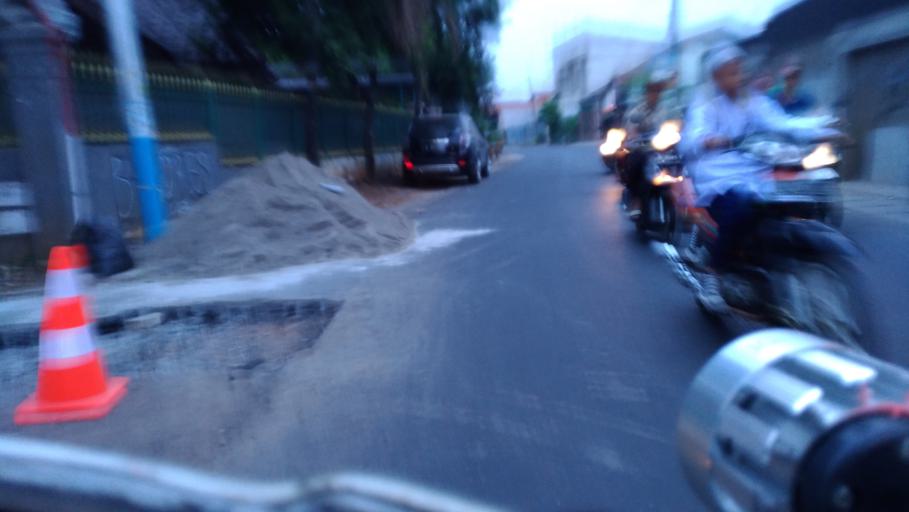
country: ID
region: West Java
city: Depok
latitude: -6.3624
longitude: 106.8845
